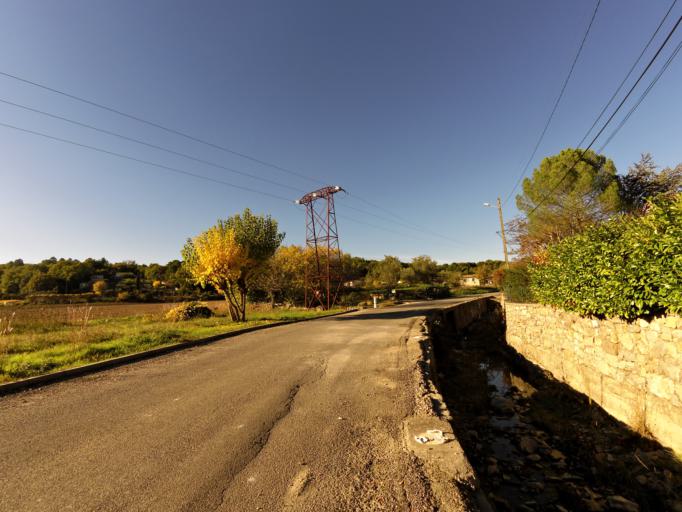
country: FR
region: Languedoc-Roussillon
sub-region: Departement du Gard
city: Sauve
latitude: 43.9895
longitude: 3.9503
